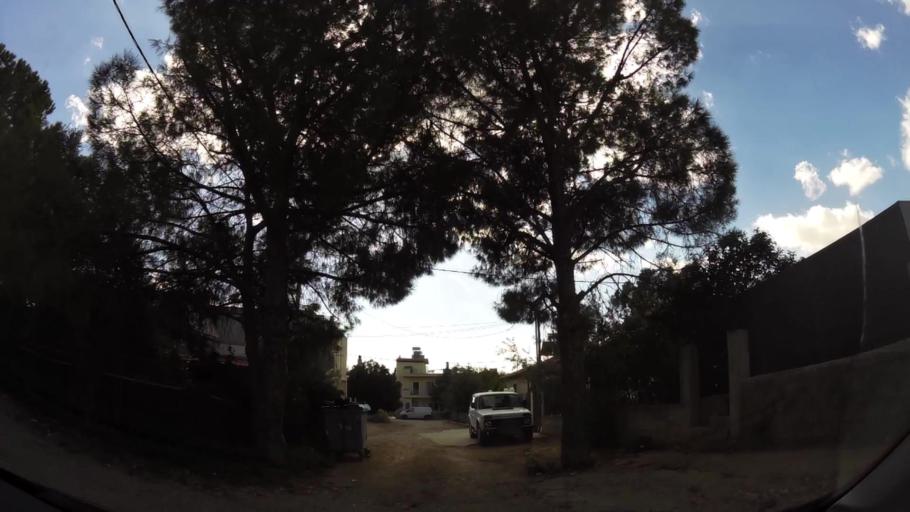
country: GR
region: Attica
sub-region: Nomarchia Anatolikis Attikis
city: Acharnes
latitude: 38.1041
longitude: 23.7470
